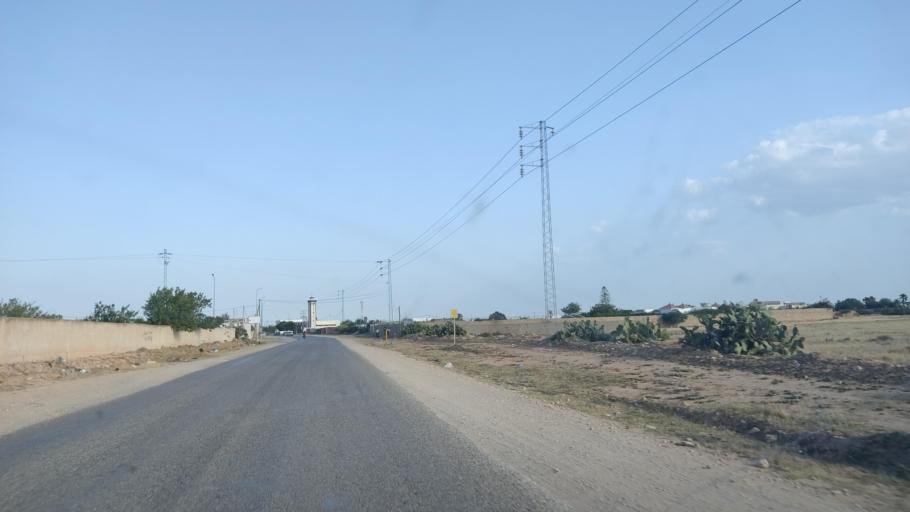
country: TN
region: Safaqis
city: Sfax
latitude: 34.8035
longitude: 10.6703
